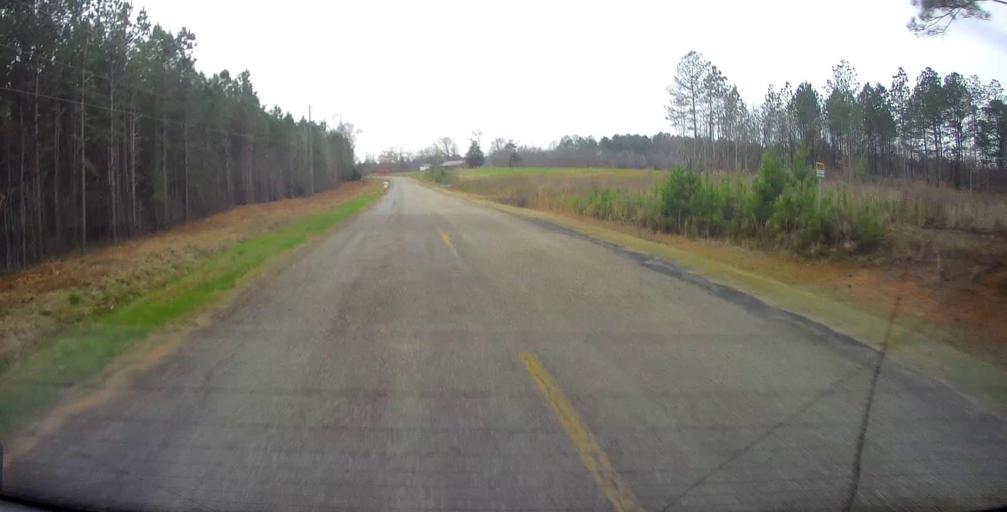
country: US
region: Georgia
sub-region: Monroe County
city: Forsyth
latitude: 33.0001
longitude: -83.8338
